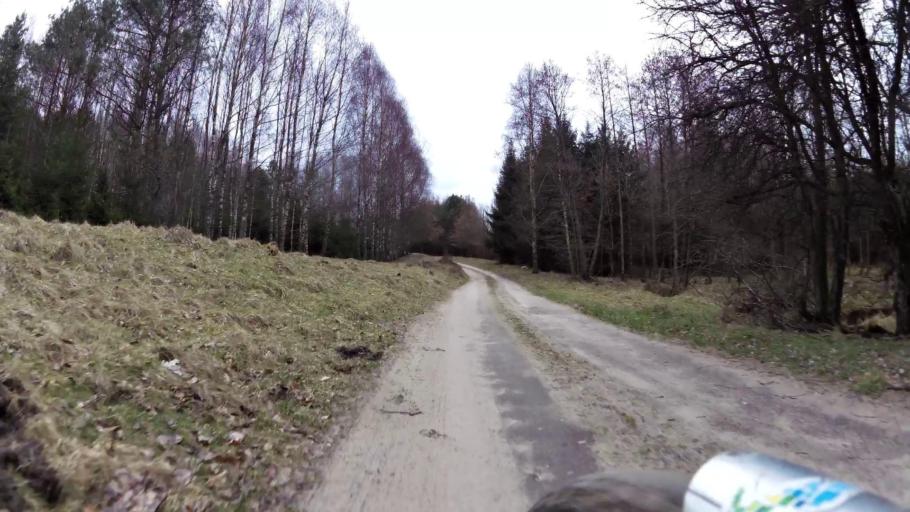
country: PL
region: Pomeranian Voivodeship
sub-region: Powiat bytowski
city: Trzebielino
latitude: 54.1155
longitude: 17.1282
